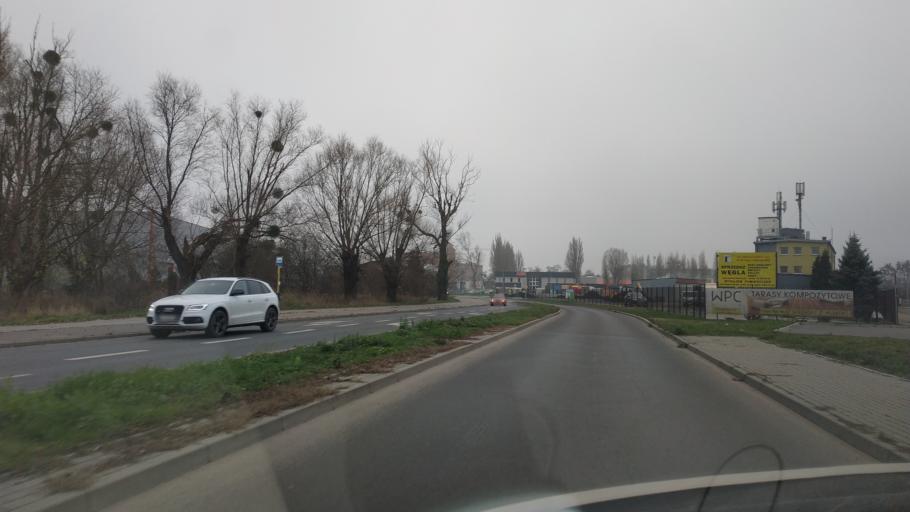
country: PL
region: Kujawsko-Pomorskie
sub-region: Torun
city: Torun
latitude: 53.0300
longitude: 18.6227
